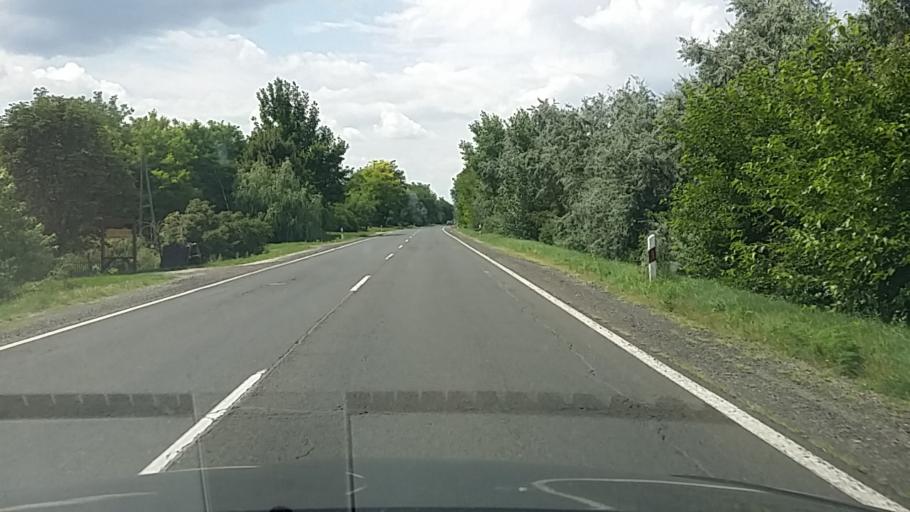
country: HU
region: Bacs-Kiskun
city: Lajosmizse
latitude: 47.0490
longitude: 19.5251
